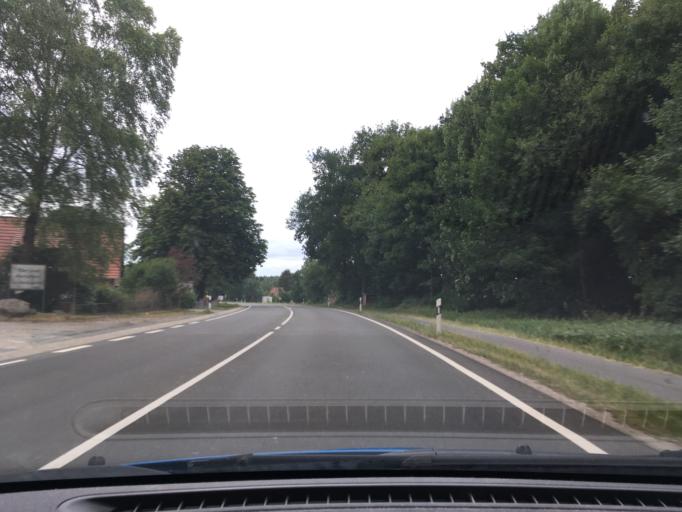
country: DE
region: Lower Saxony
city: Drestedt
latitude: 53.3287
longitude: 9.8132
